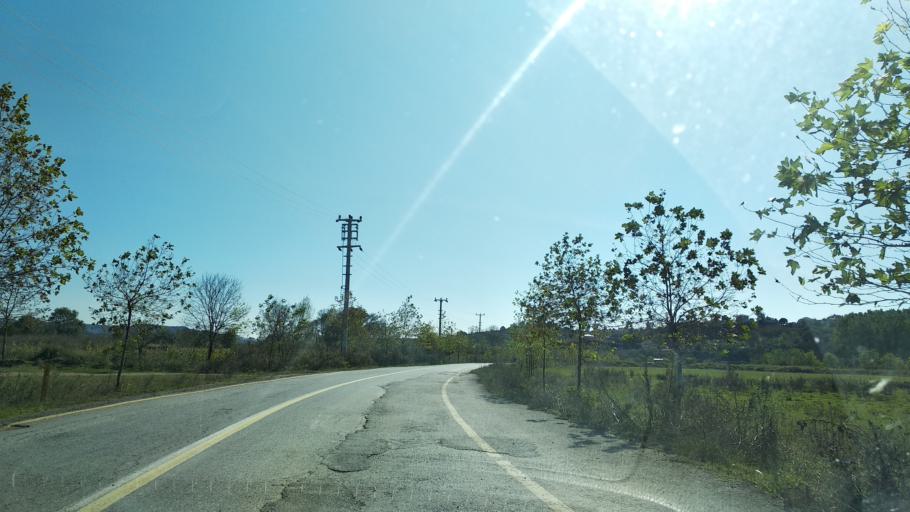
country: TR
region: Sakarya
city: Karasu
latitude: 41.1125
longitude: 30.6435
